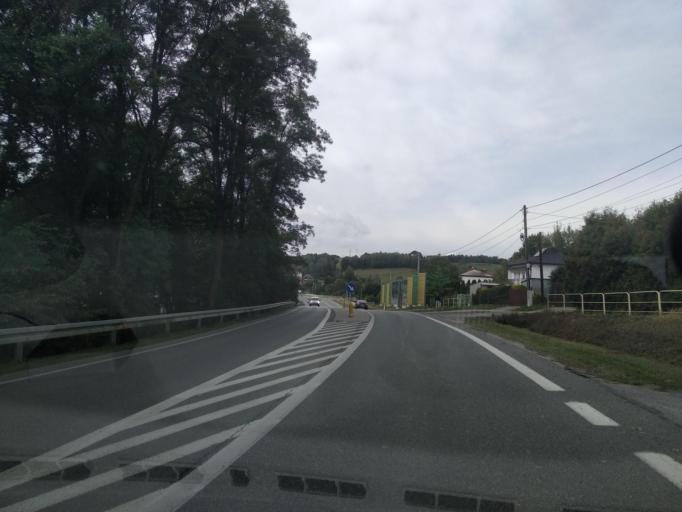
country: PL
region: Subcarpathian Voivodeship
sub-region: Powiat jasielski
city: Skolyszyn
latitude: 49.7574
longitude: 21.3021
